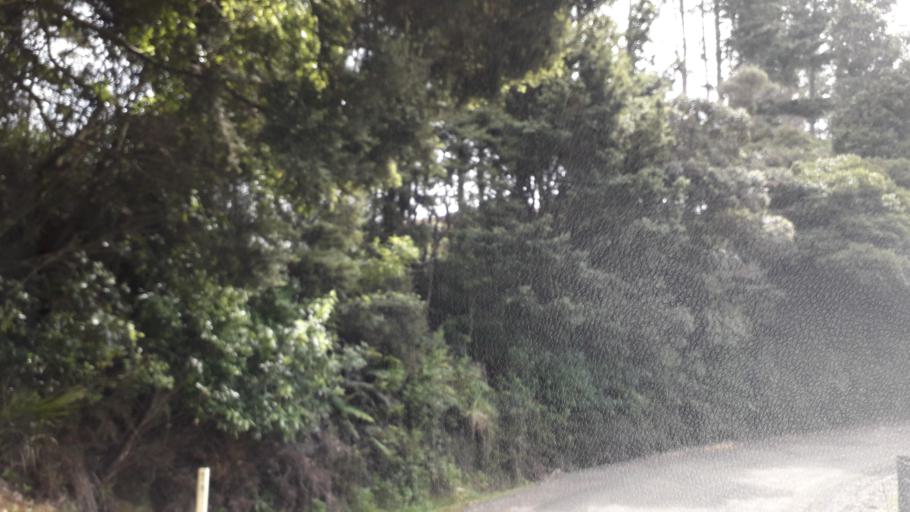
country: NZ
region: Northland
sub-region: Far North District
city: Kaitaia
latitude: -35.2275
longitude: 173.2726
